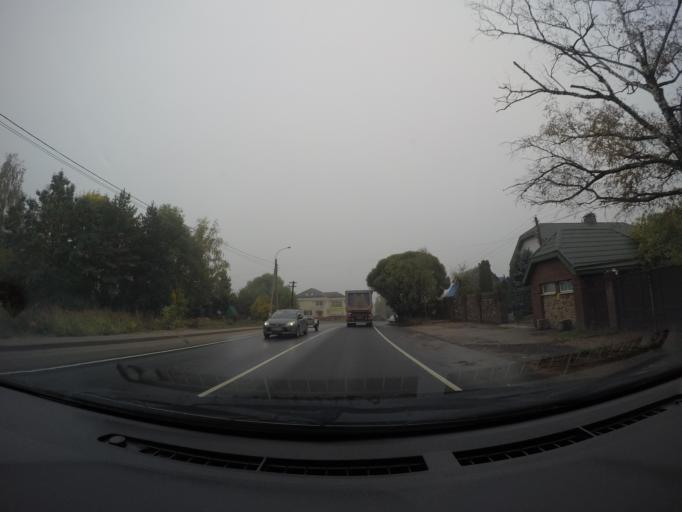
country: RU
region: Moskovskaya
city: Rumyantsevo
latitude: 55.8517
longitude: 36.5076
